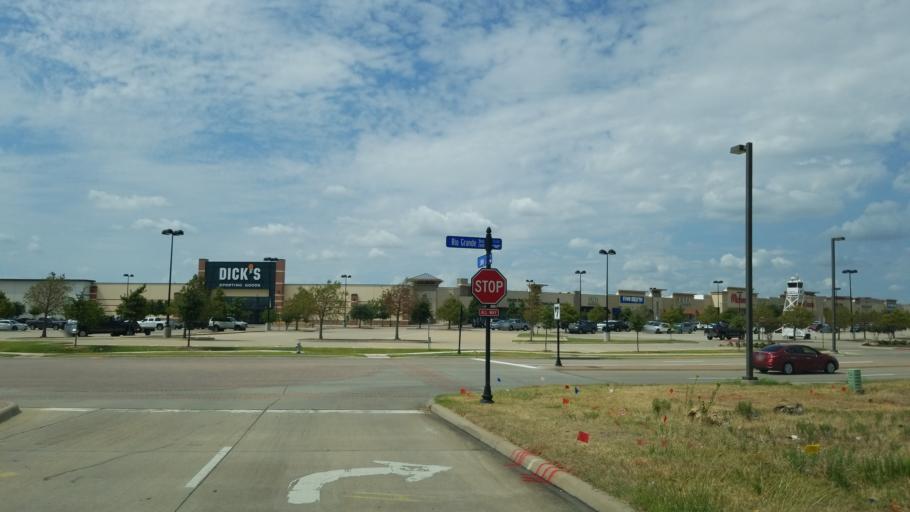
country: US
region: Texas
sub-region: Tarrant County
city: Euless
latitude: 32.8776
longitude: -97.1009
